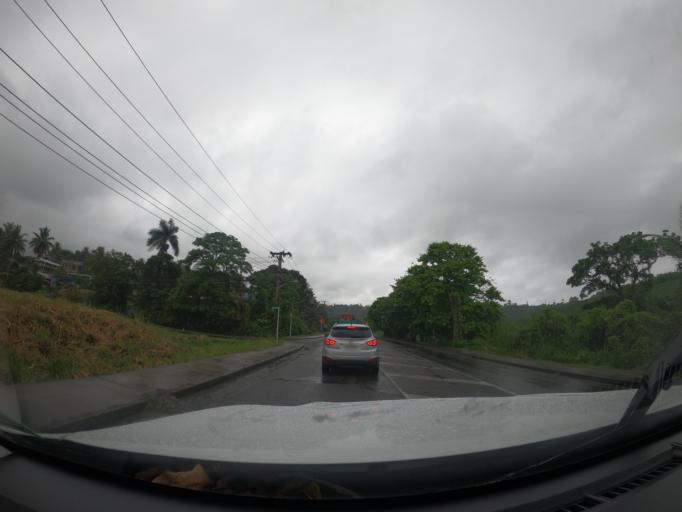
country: FJ
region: Central
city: Suva
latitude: -18.1134
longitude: 178.4278
